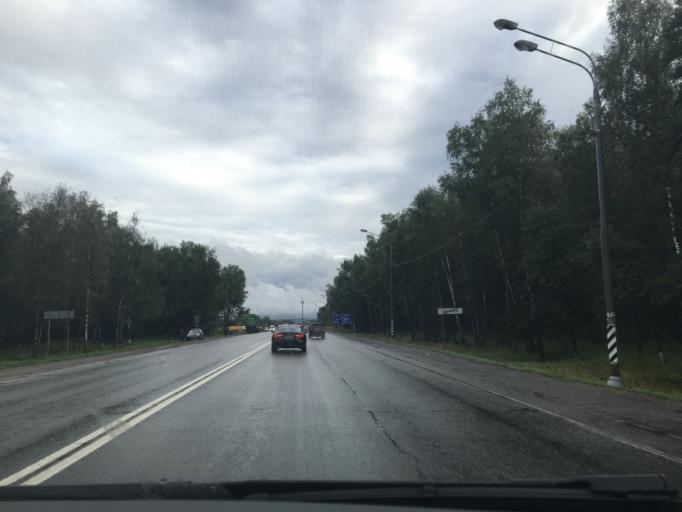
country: RU
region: Kaluga
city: Obninsk
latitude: 55.0819
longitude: 36.6305
